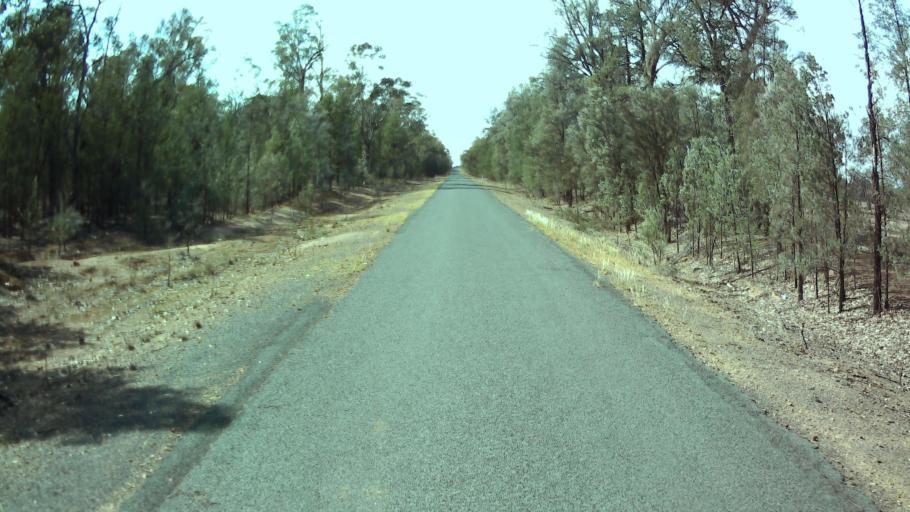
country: AU
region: New South Wales
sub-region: Weddin
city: Grenfell
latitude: -33.7265
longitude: 148.0323
